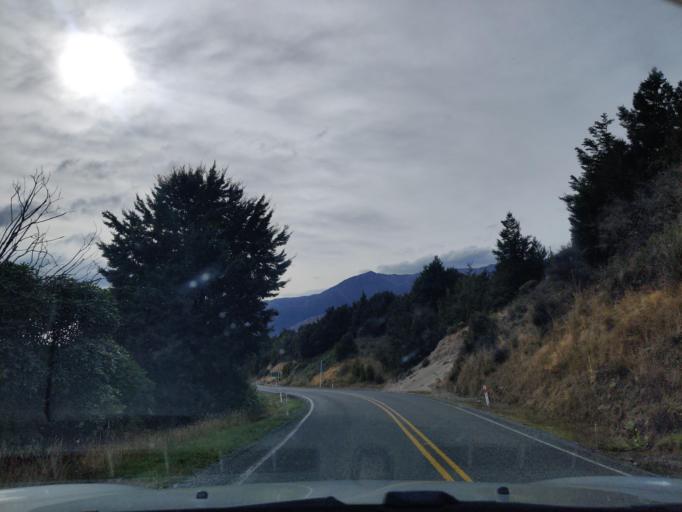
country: NZ
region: Tasman
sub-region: Tasman District
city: Wakefield
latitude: -41.7693
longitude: 172.9450
